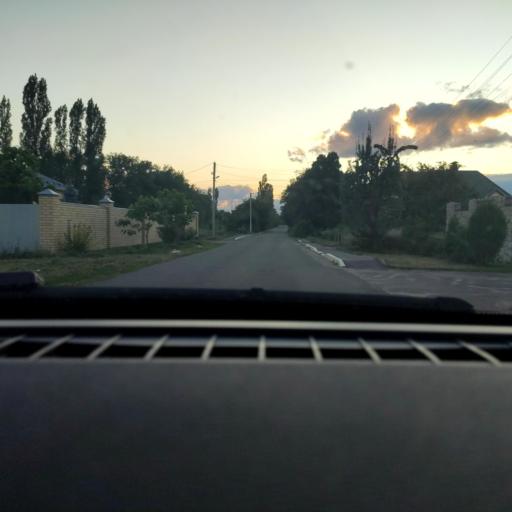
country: RU
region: Voronezj
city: Novaya Usman'
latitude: 51.6560
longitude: 39.3339
